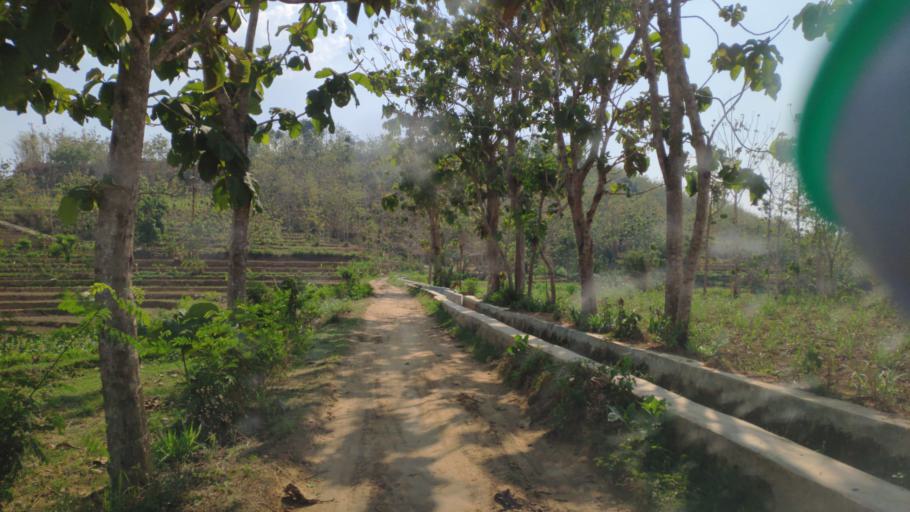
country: ID
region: Central Java
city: Ngapus
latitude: -6.9353
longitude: 111.2131
